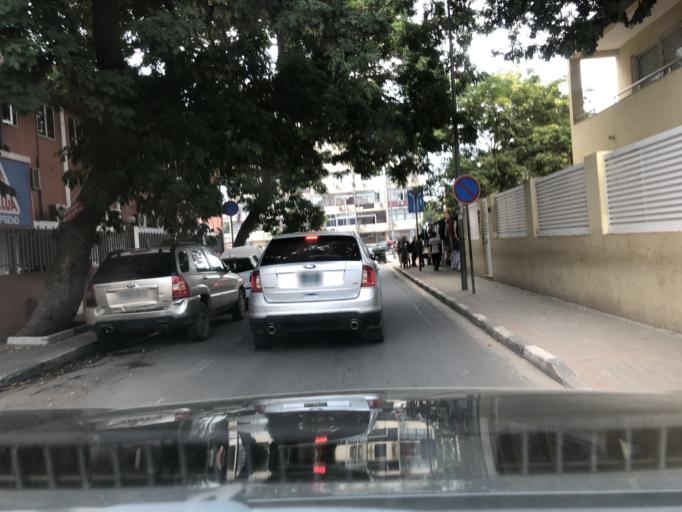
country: AO
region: Luanda
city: Luanda
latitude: -8.8229
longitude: 13.2508
